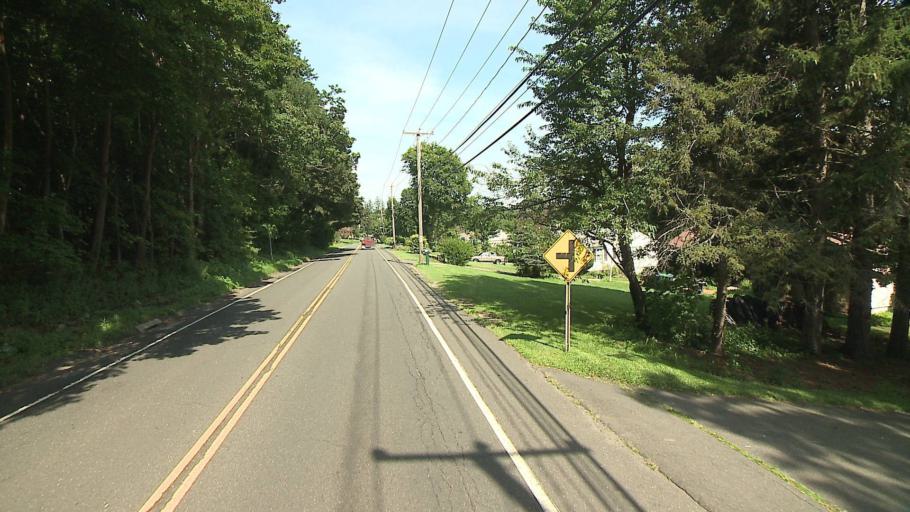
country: US
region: Connecticut
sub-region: Fairfield County
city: Danbury
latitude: 41.4261
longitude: -73.4833
